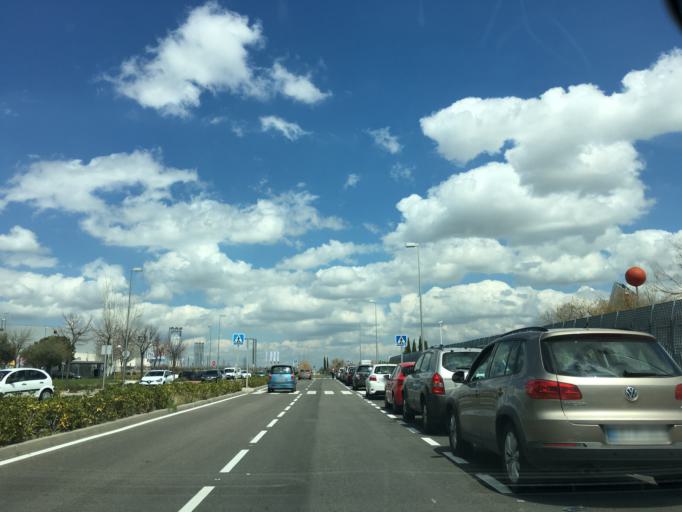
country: ES
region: Madrid
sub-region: Provincia de Madrid
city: San Blas
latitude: 40.4629
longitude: -3.6134
